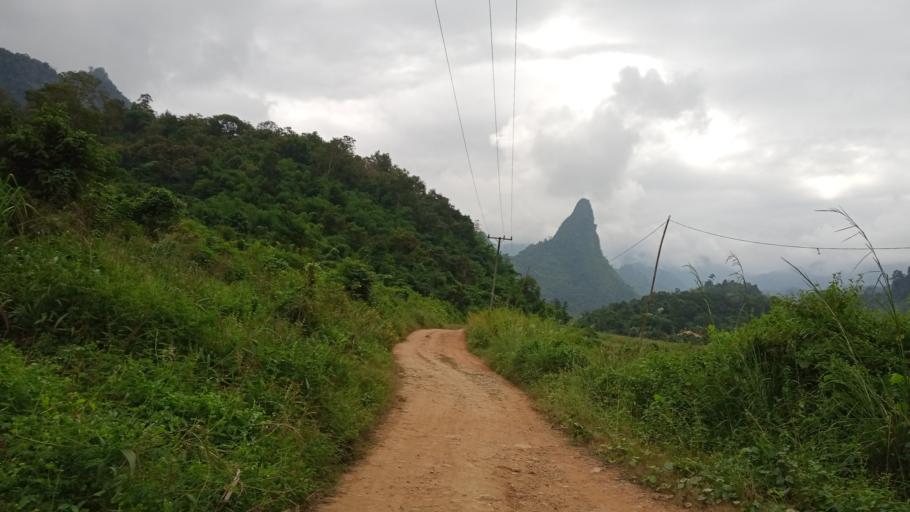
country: LA
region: Xiangkhoang
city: Phonsavan
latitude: 19.0864
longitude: 103.0088
